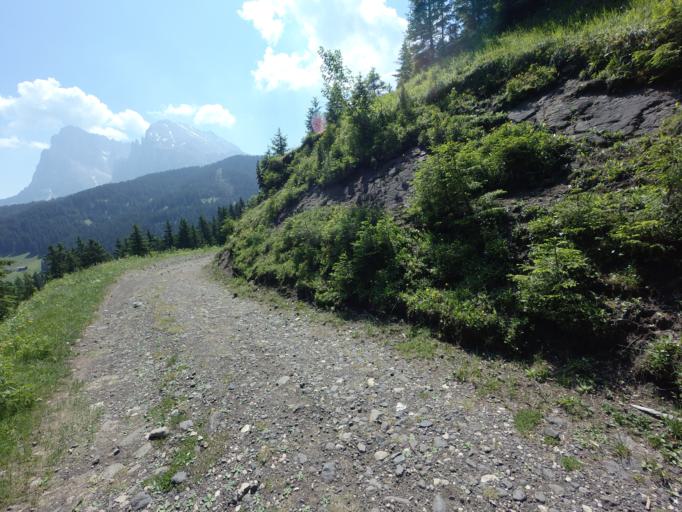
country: IT
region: Trentino-Alto Adige
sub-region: Bolzano
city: Ortisei
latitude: 46.5210
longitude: 11.6605
